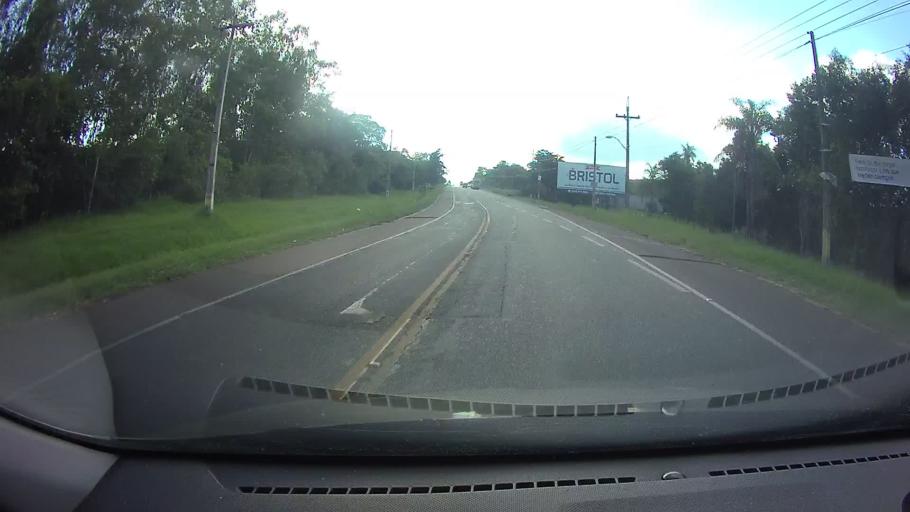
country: PY
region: Cordillera
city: Caacupe
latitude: -25.3883
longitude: -57.0845
